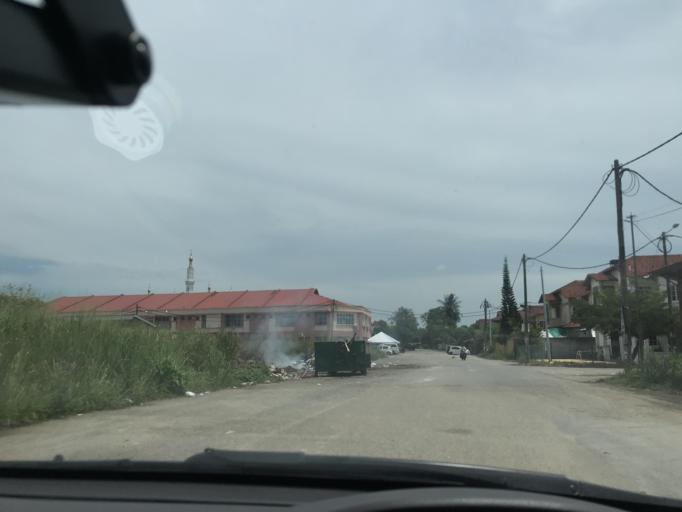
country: MY
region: Kelantan
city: Kota Bharu
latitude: 6.1208
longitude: 102.2190
